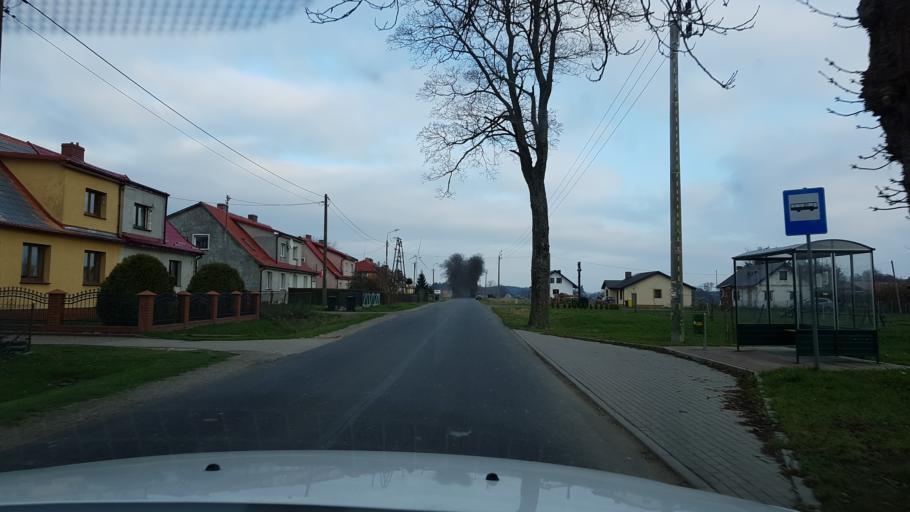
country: PL
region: West Pomeranian Voivodeship
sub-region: Powiat kolobrzeski
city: Goscino
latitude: 54.0553
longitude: 15.6718
